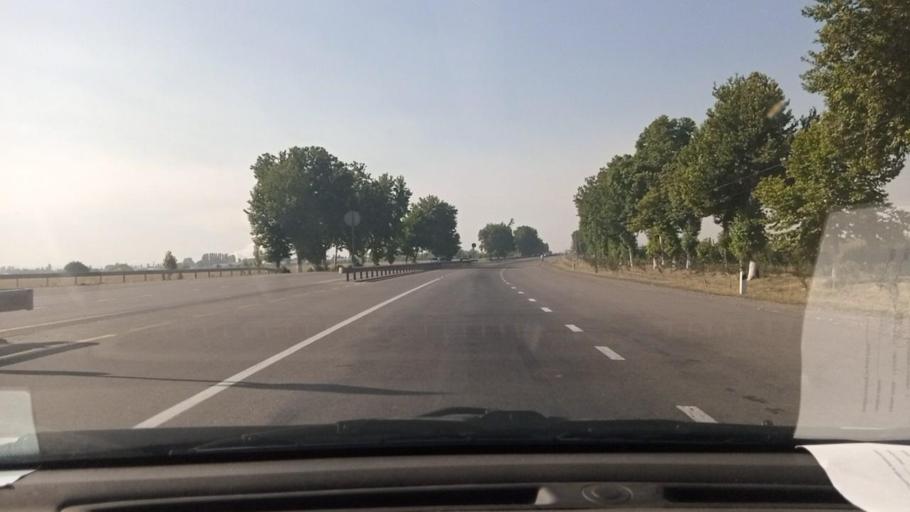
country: UZ
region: Toshkent Shahri
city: Bektemir
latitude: 41.1441
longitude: 69.4318
